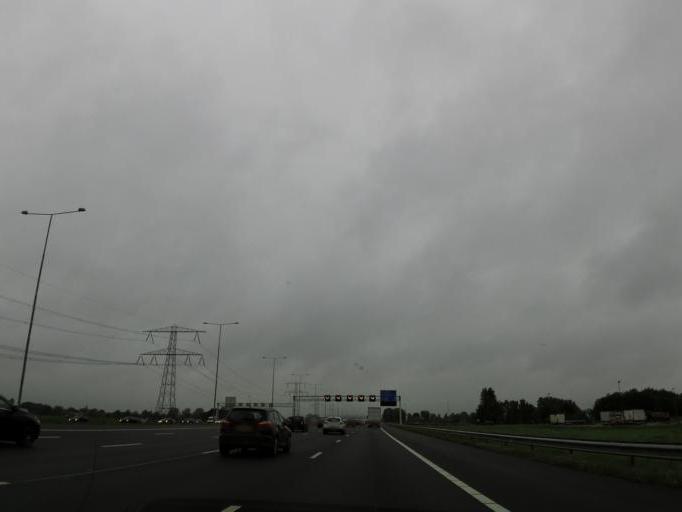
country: NL
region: Utrecht
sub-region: Stichtse Vecht
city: Breukelen
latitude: 52.1830
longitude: 4.9867
